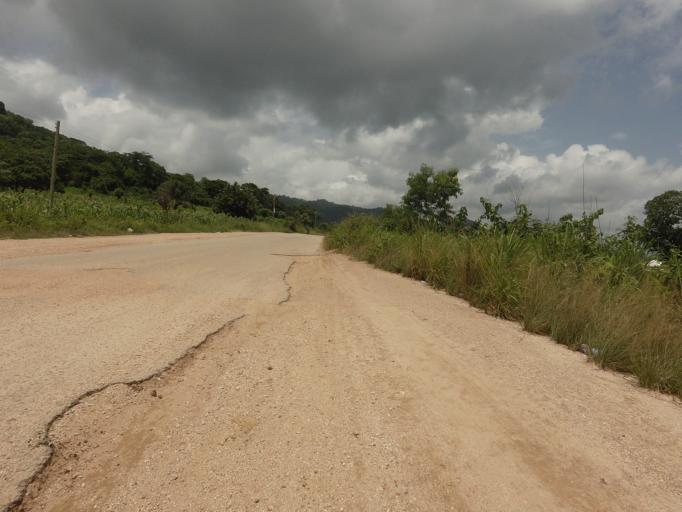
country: GH
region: Volta
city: Ho
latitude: 6.6997
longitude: 0.3351
